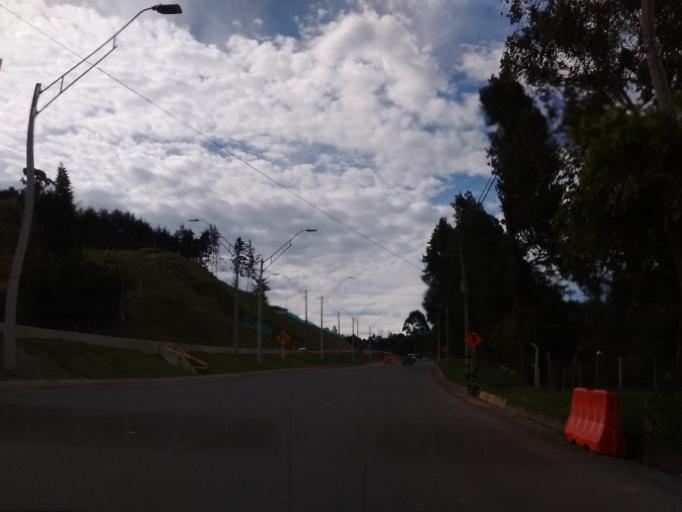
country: CO
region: Antioquia
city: Marinilla
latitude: 6.1621
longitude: -75.3191
